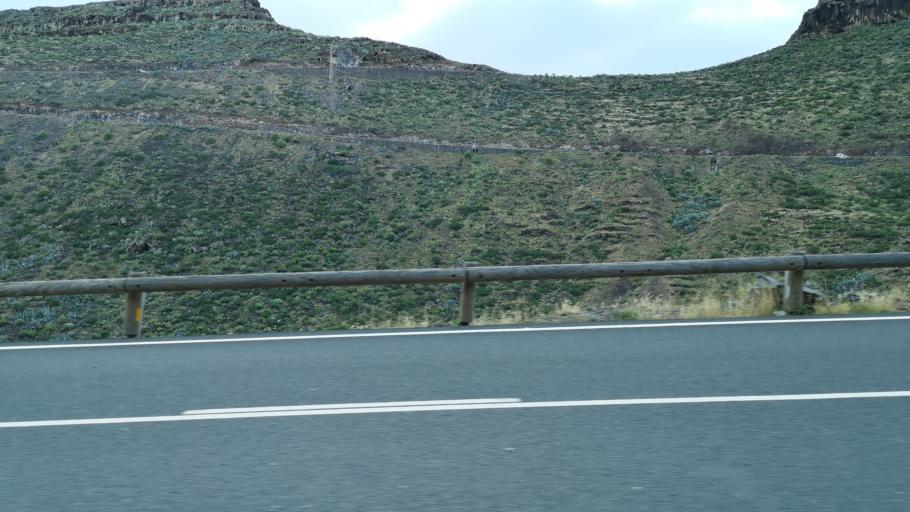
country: ES
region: Canary Islands
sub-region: Provincia de Santa Cruz de Tenerife
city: San Sebastian de la Gomera
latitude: 28.0875
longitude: -17.1259
